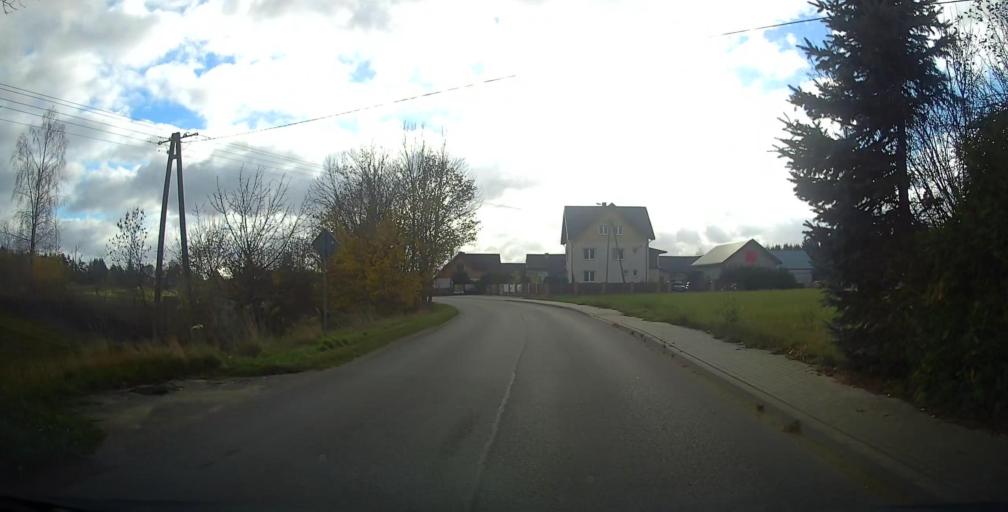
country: PL
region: Podlasie
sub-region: Suwalki
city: Suwalki
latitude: 54.2914
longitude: 22.8790
